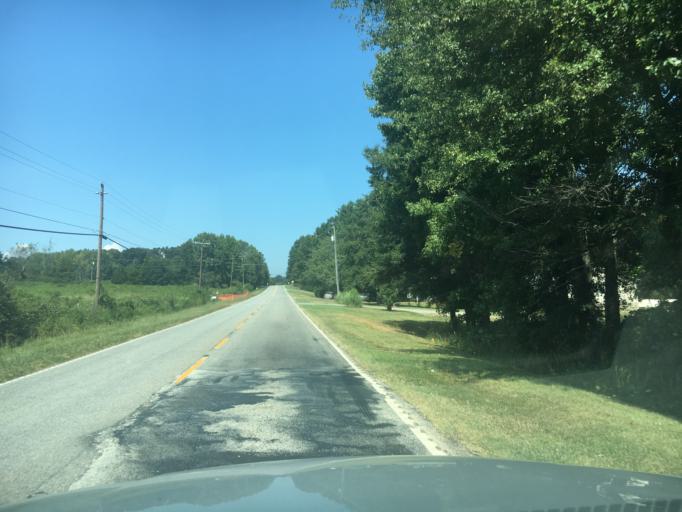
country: US
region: South Carolina
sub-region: Spartanburg County
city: Boiling Springs
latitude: 35.1264
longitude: -82.0332
